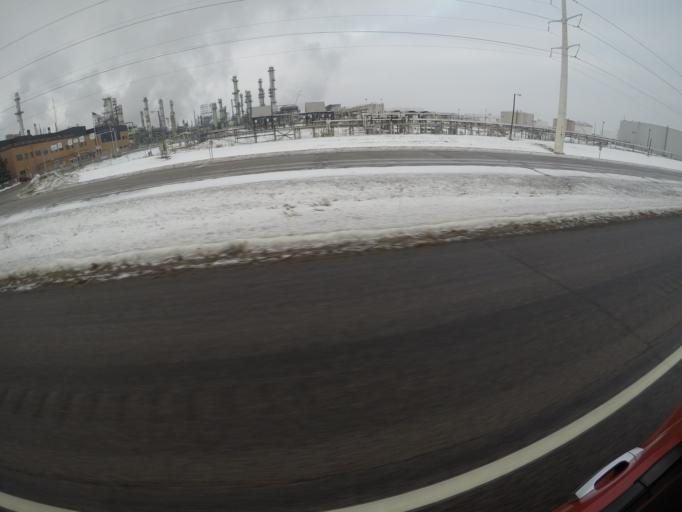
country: US
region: Minnesota
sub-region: Dakota County
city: Inver Grove Heights
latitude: 44.7686
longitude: -93.0348
